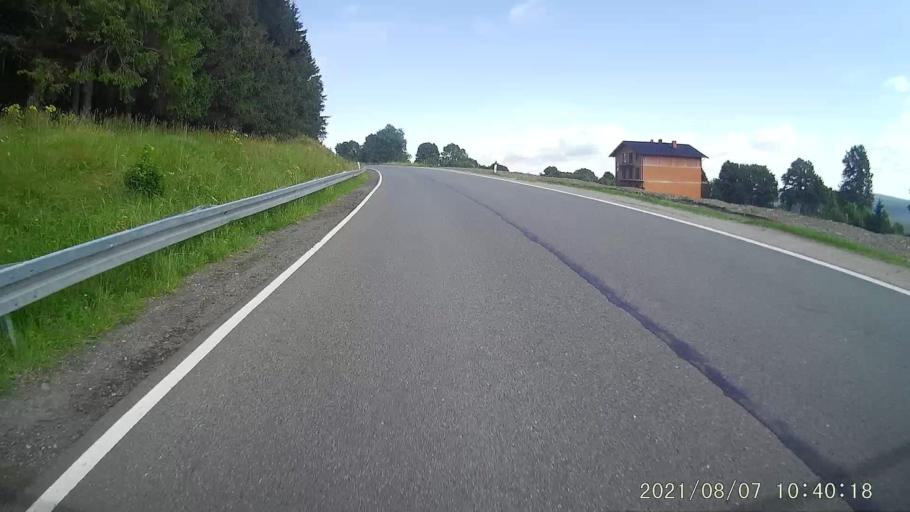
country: PL
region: Lower Silesian Voivodeship
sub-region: Powiat klodzki
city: Duszniki-Zdroj
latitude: 50.3452
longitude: 16.3832
